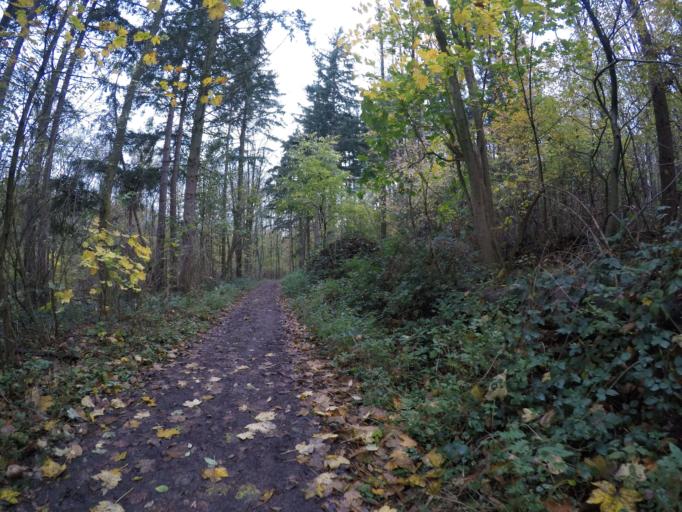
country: BE
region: Flanders
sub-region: Provincie West-Vlaanderen
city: Saint-Yvon
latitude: 50.7876
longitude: 2.8772
